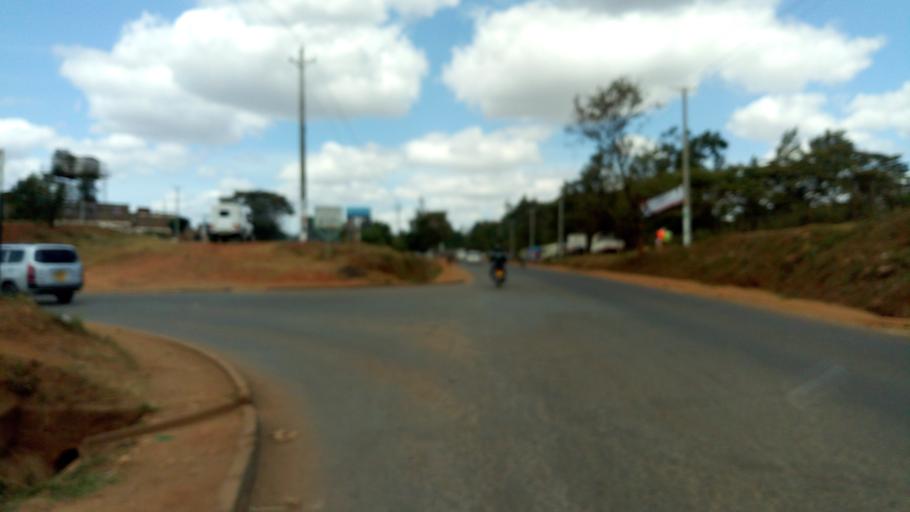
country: KE
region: Nairobi Area
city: Nairobi
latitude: -1.3304
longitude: 36.7804
